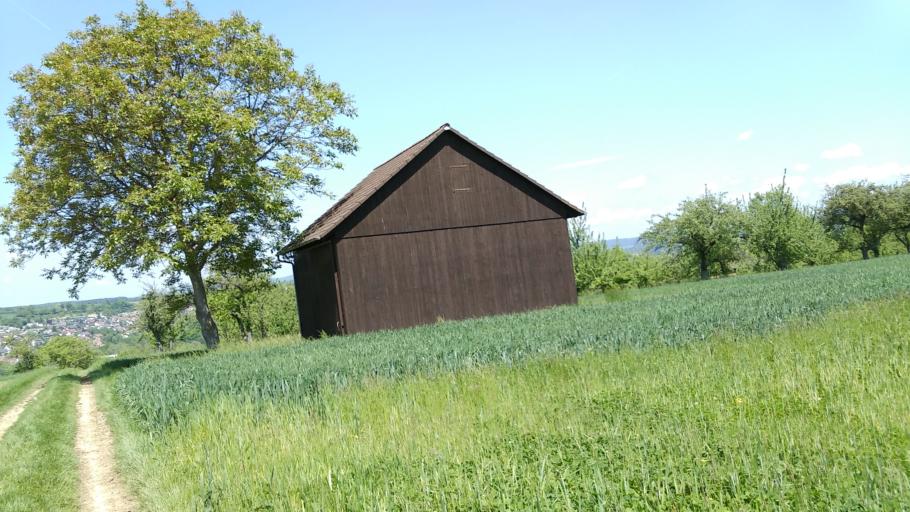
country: DE
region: Baden-Wuerttemberg
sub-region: Regierungsbezirk Stuttgart
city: Nurtingen
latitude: 48.6325
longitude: 9.3546
